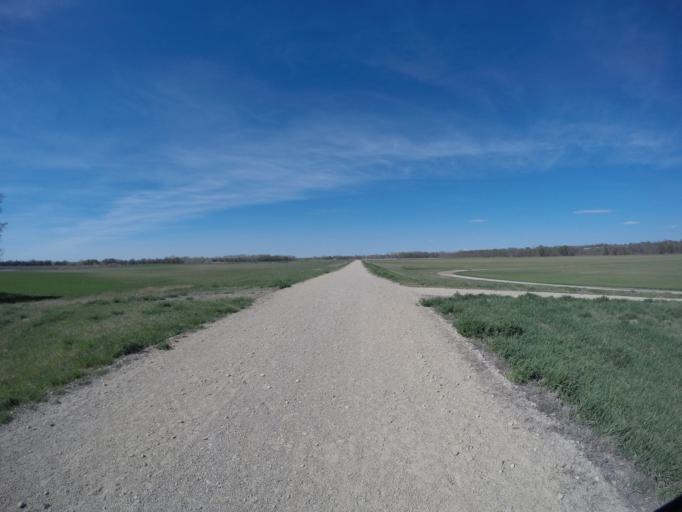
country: US
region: Kansas
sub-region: Saline County
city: Salina
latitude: 38.7862
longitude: -97.5761
